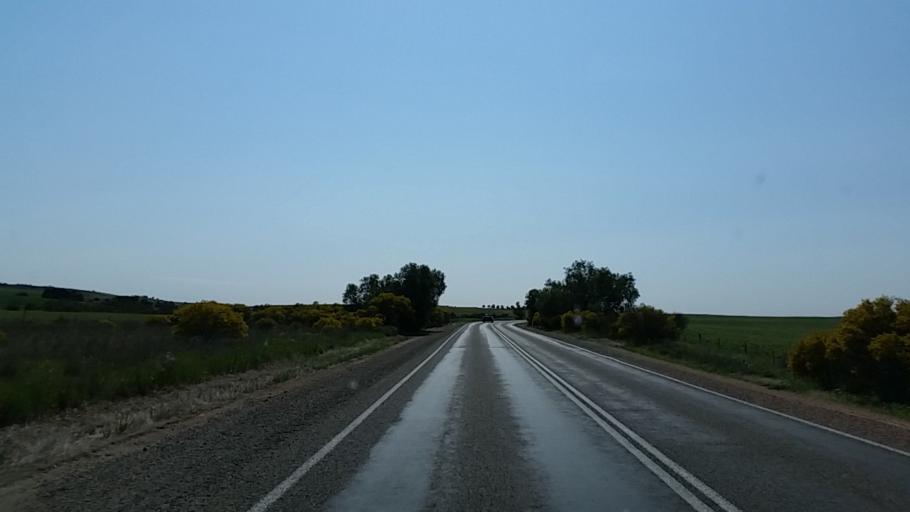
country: AU
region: South Australia
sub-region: Northern Areas
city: Jamestown
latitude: -33.2121
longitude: 138.4229
